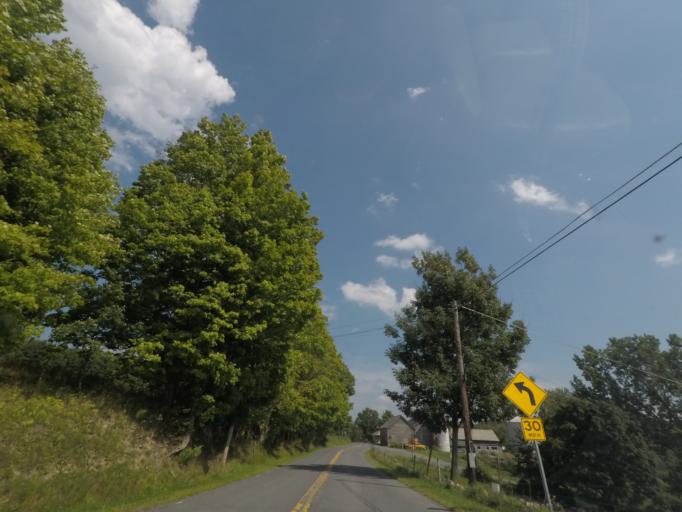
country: US
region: New York
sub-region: Saratoga County
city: Waterford
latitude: 42.8075
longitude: -73.5907
